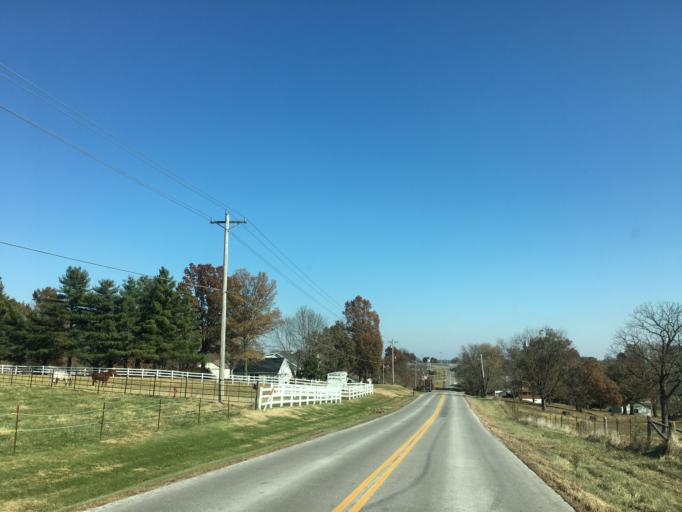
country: US
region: Missouri
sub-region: Cole County
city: Wardsville
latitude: 38.4866
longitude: -92.1826
